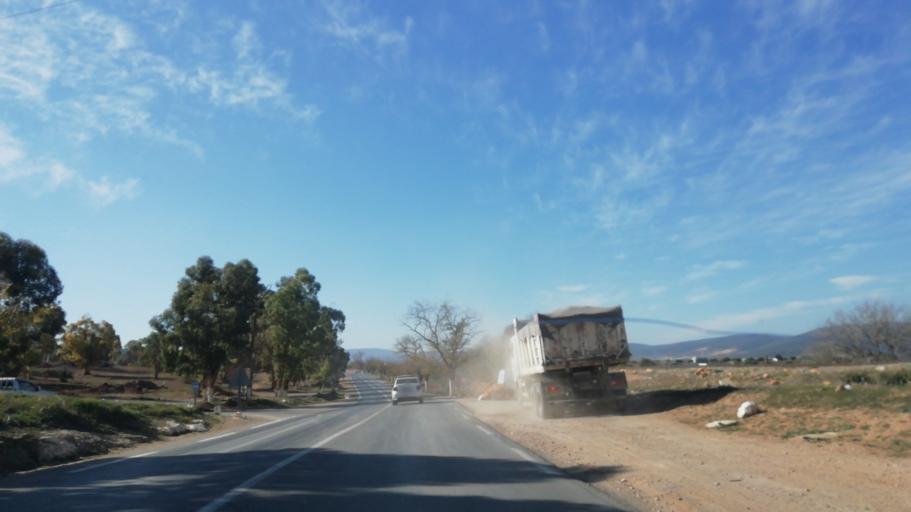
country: DZ
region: Tlemcen
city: Ouled Mimoun
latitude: 34.8977
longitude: -1.0543
